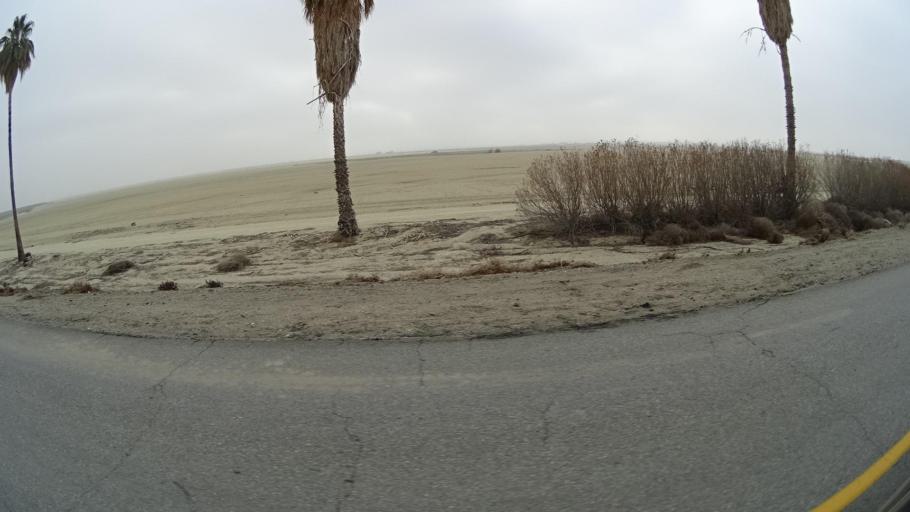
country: US
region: California
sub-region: Kern County
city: Maricopa
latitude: 35.1211
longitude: -119.3593
